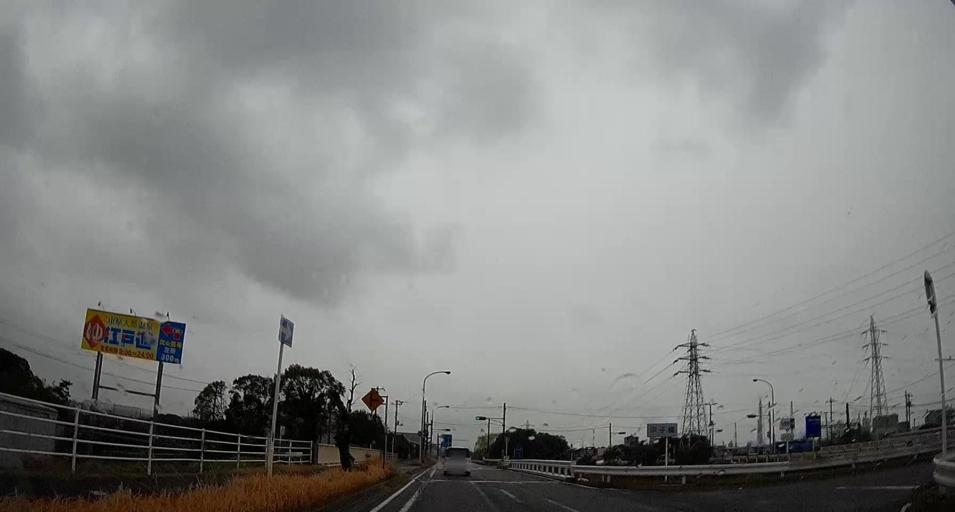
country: JP
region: Chiba
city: Ichihara
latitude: 35.5236
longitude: 140.0641
